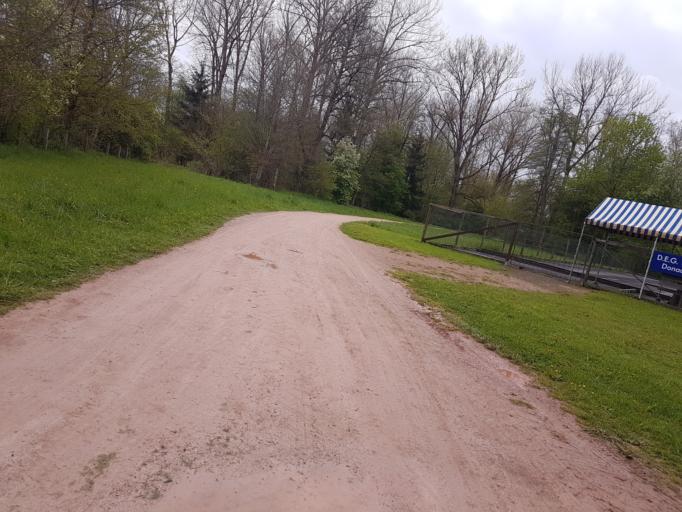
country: DE
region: Baden-Wuerttemberg
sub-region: Freiburg Region
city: Donaueschingen
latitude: 47.9475
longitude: 8.5076
